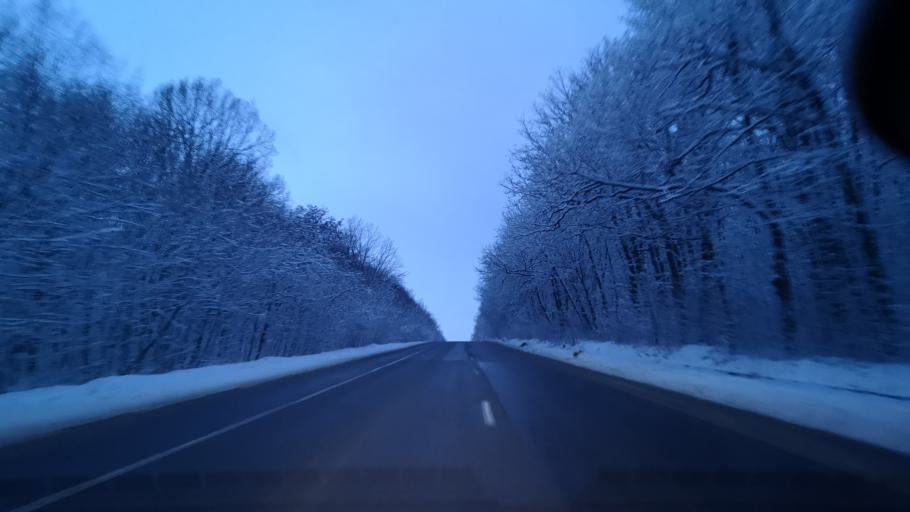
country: MD
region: Rezina
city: Rezina
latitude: 47.7261
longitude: 28.8604
